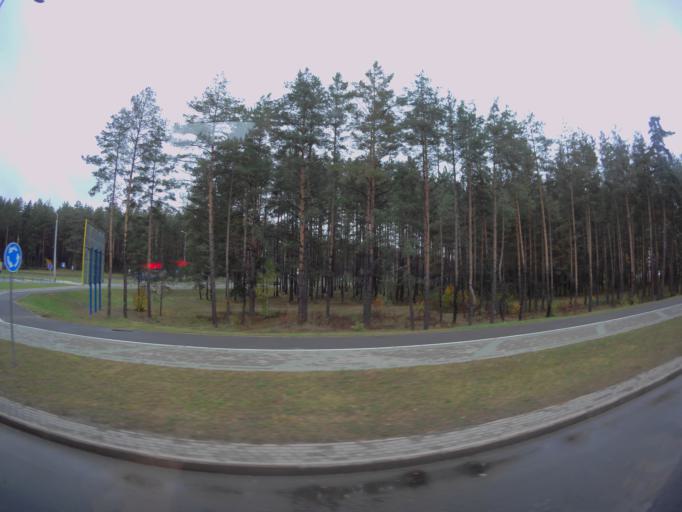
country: BY
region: Minsk
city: Horad Barysaw
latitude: 54.1970
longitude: 28.4711
